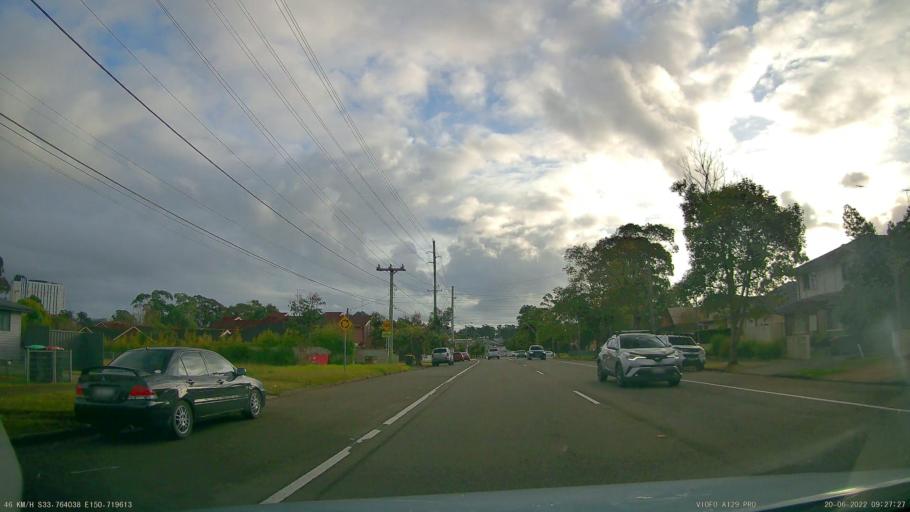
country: AU
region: New South Wales
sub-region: Penrith Municipality
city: Kingswood Park
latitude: -33.7639
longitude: 150.7197
